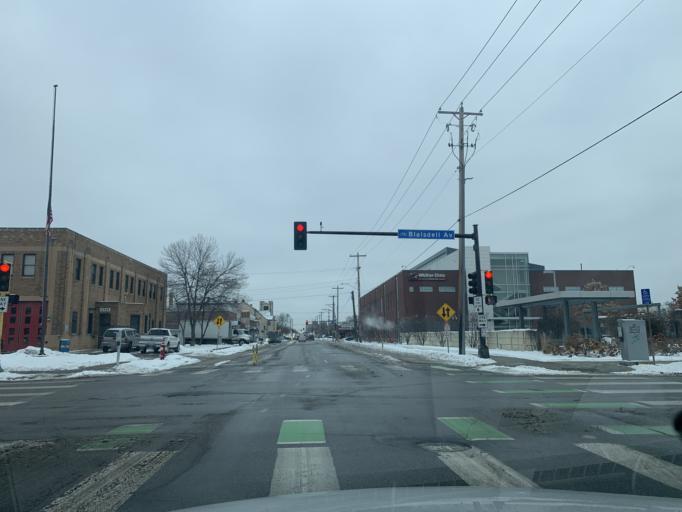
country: US
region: Minnesota
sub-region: Hennepin County
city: Minneapolis
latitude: 44.9520
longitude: -93.2799
